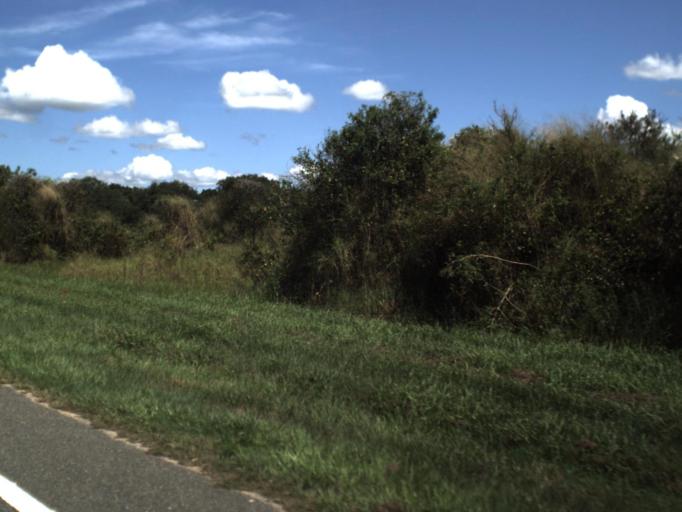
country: US
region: Florida
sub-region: Polk County
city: Lake Wales
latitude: 27.9484
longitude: -81.5948
